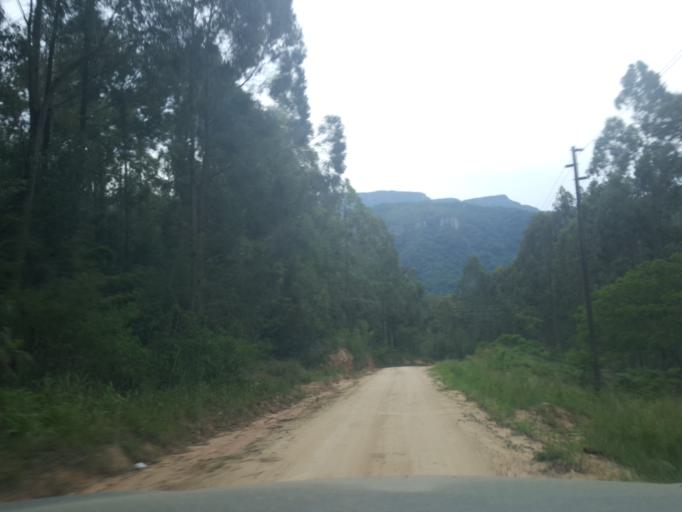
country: ZA
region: Limpopo
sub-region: Mopani District Municipality
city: Hoedspruit
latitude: -24.5947
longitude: 30.8793
